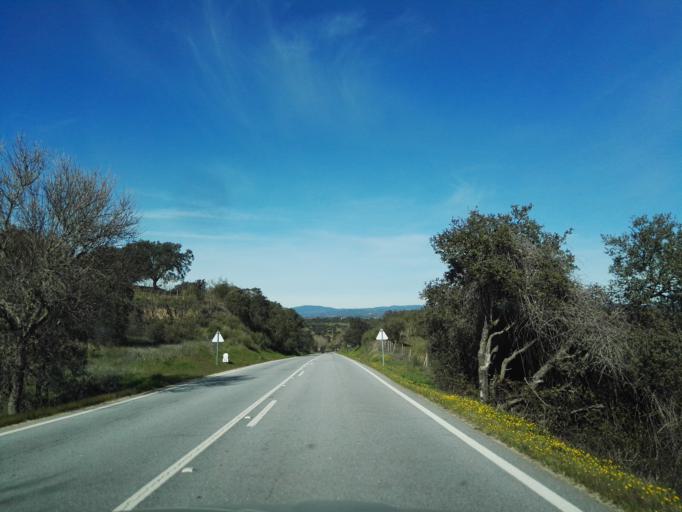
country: PT
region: Portalegre
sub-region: Arronches
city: Arronches
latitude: 39.0857
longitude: -7.2825
